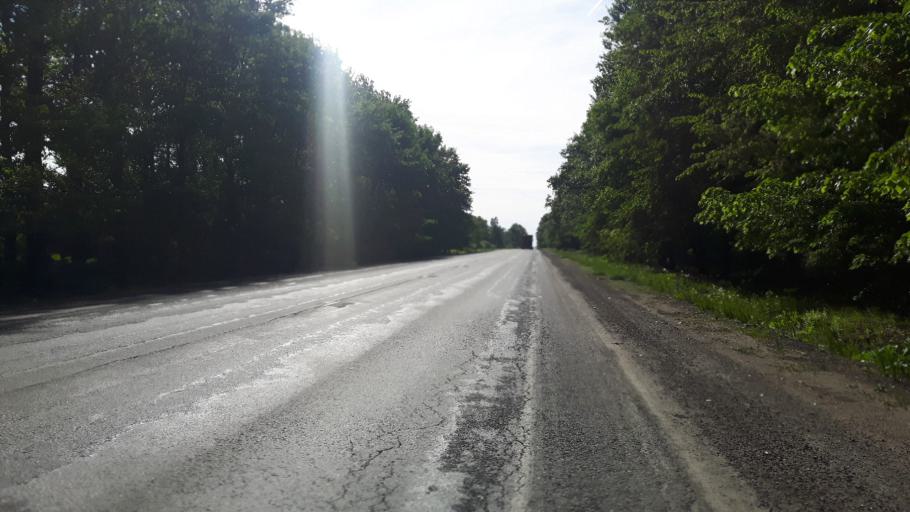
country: RU
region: Leningrad
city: Ivangorod
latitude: 59.3818
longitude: 28.3527
